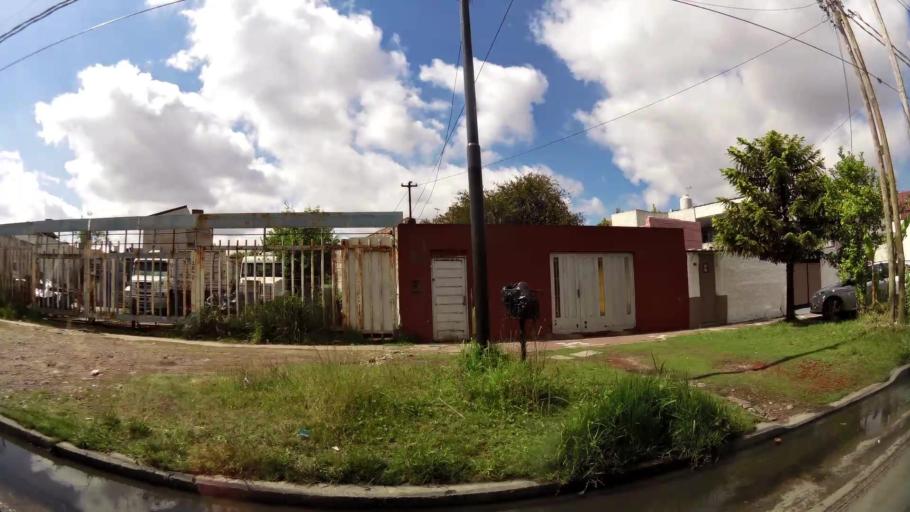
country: AR
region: Buenos Aires
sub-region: Partido de Lanus
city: Lanus
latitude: -34.6860
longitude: -58.4111
